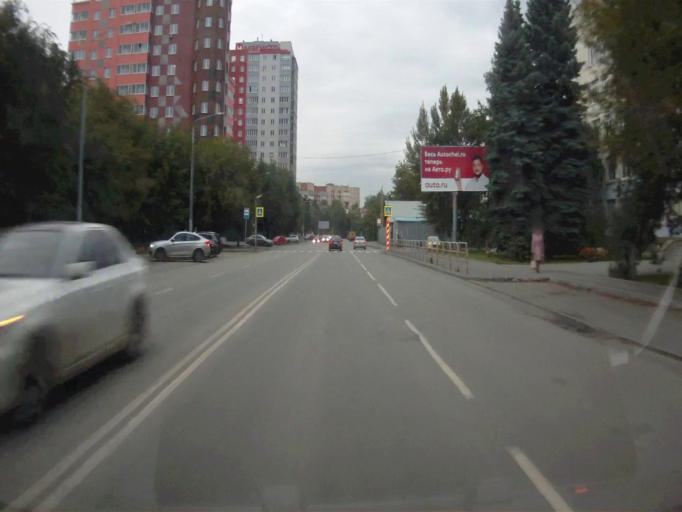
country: RU
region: Chelyabinsk
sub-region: Gorod Chelyabinsk
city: Chelyabinsk
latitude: 55.1509
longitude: 61.3985
